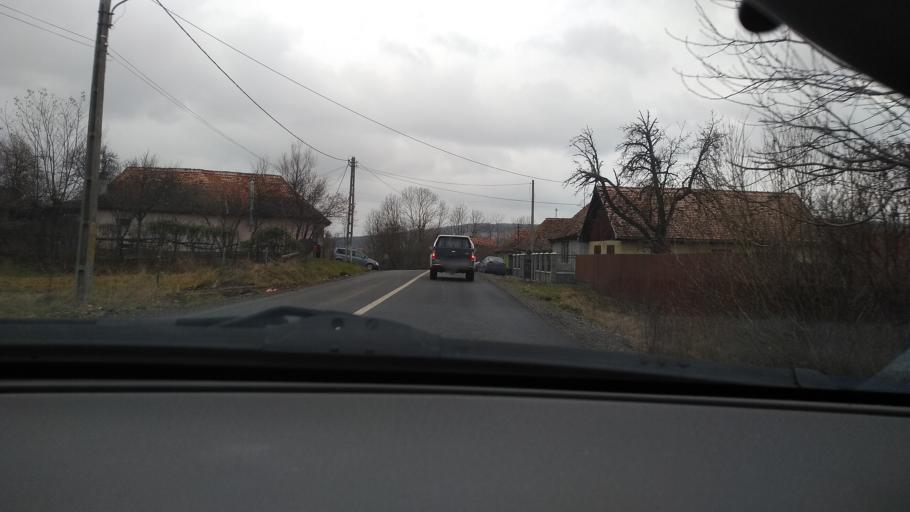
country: RO
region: Mures
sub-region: Comuna Bereni
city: Bereni
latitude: 46.5582
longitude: 24.8734
